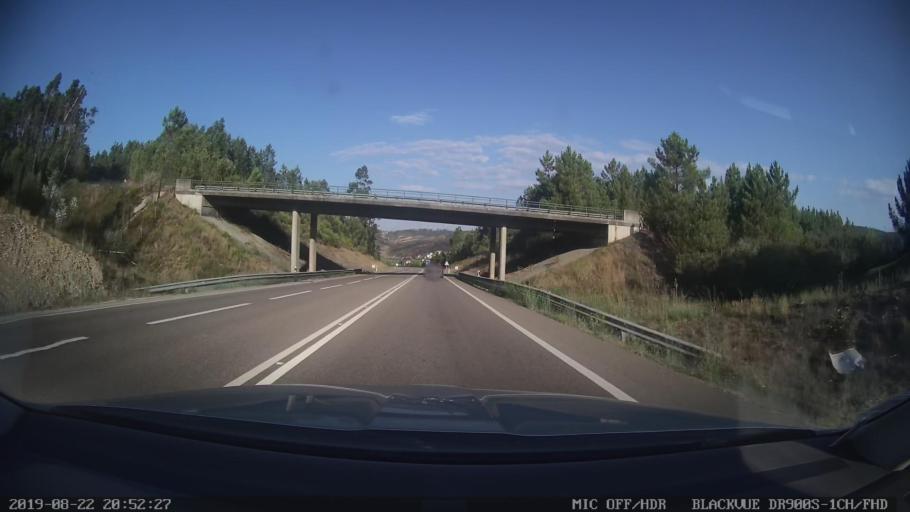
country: PT
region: Castelo Branco
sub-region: Proenca-A-Nova
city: Proenca-a-Nova
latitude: 39.7690
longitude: -7.9726
